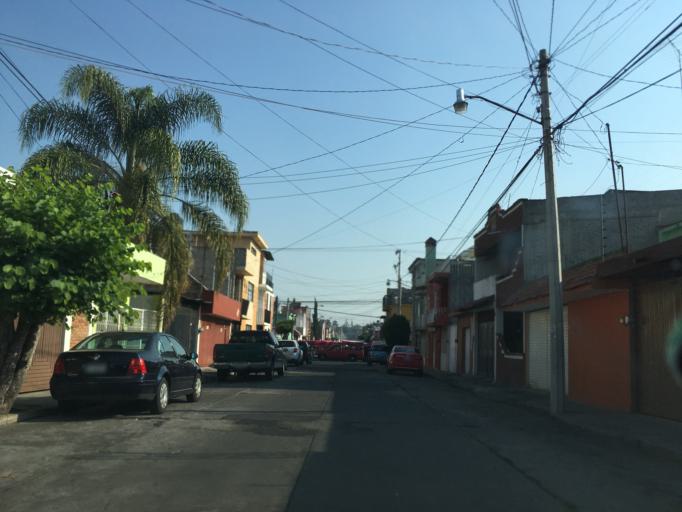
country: MX
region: Michoacan
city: Morelia
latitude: 19.6903
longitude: -101.1825
